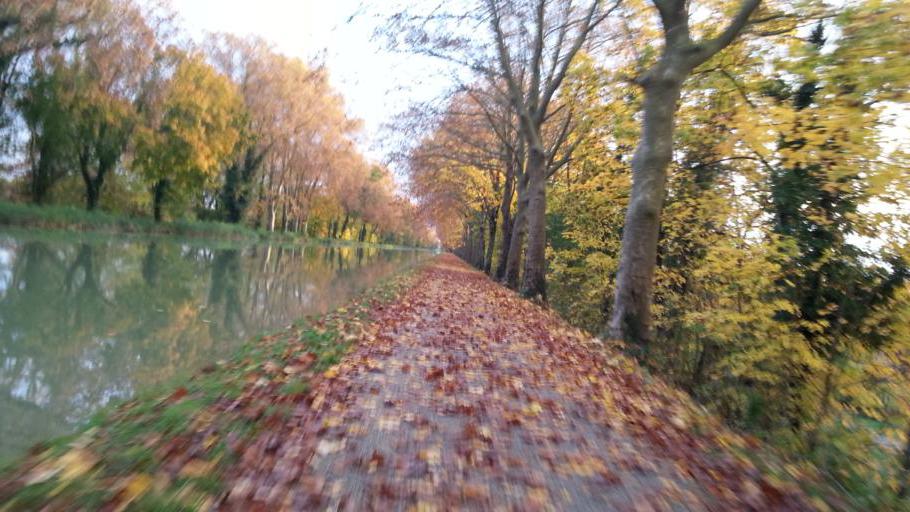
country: FR
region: Midi-Pyrenees
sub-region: Departement du Tarn-et-Garonne
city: Moissac
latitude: 44.0891
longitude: 1.1016
